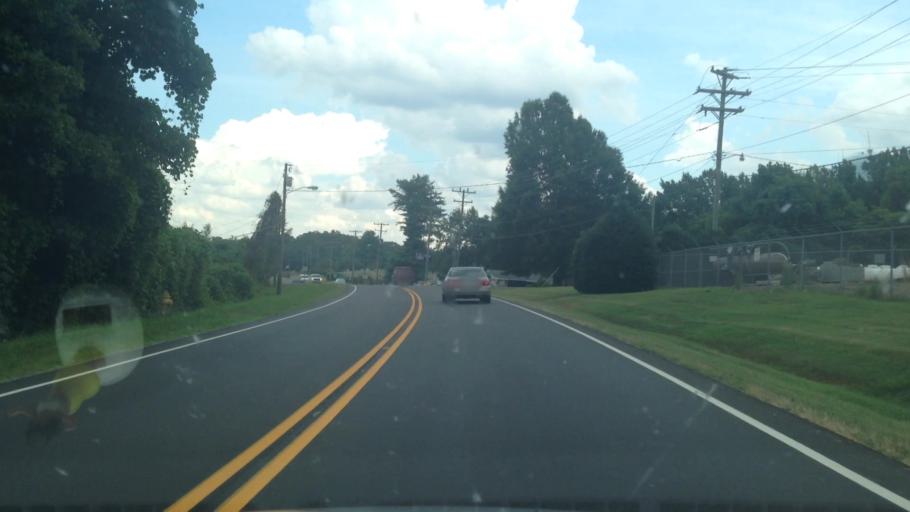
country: US
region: North Carolina
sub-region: Rockingham County
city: Madison
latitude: 36.3780
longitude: -79.9465
